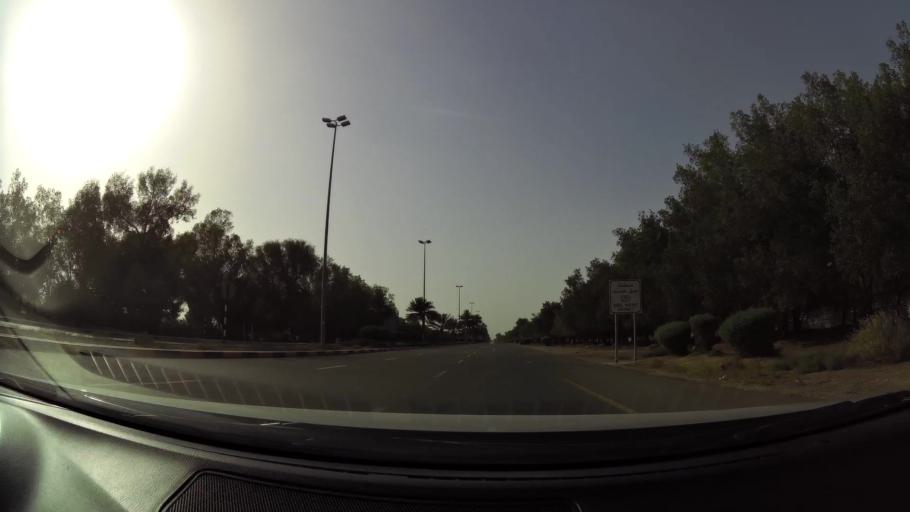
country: AE
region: Abu Dhabi
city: Al Ain
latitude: 24.0914
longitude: 55.7238
